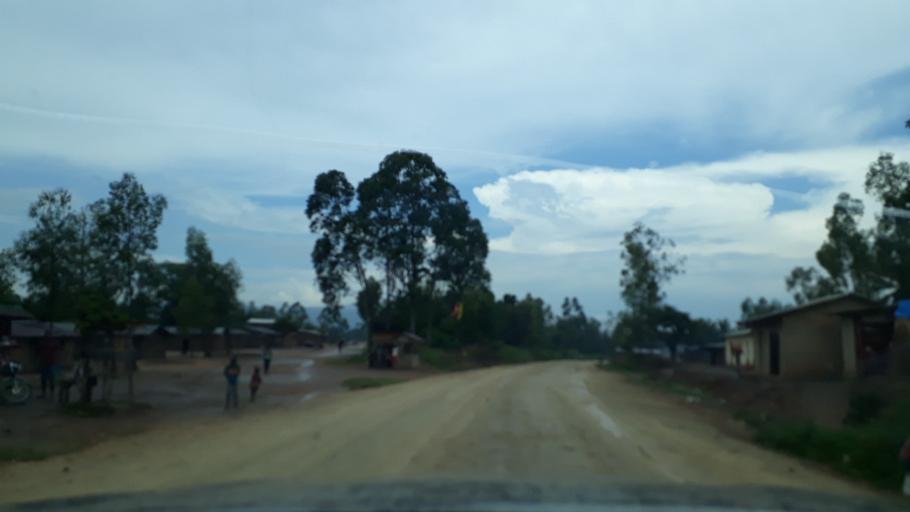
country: CD
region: Eastern Province
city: Bunia
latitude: 1.6225
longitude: 30.2686
